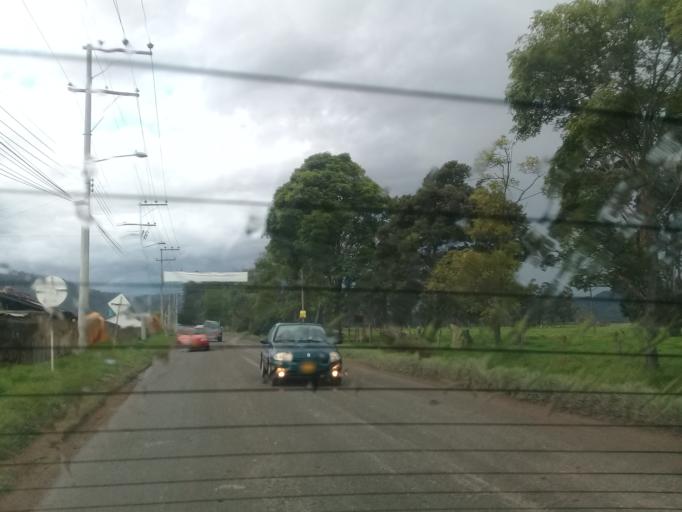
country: CO
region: Cundinamarca
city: Zipaquira
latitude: 5.0078
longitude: -73.9850
